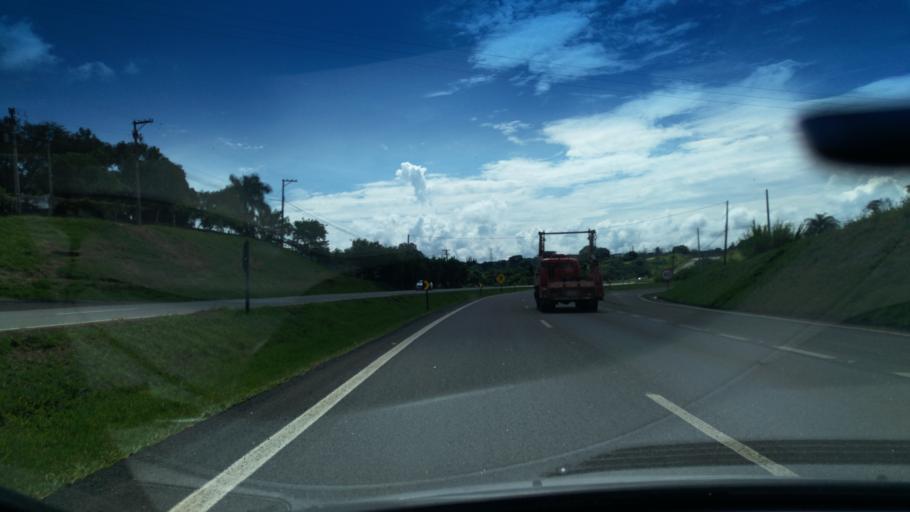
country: BR
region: Sao Paulo
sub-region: Santo Antonio Do Jardim
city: Espirito Santo do Pinhal
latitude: -22.1990
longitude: -46.7772
